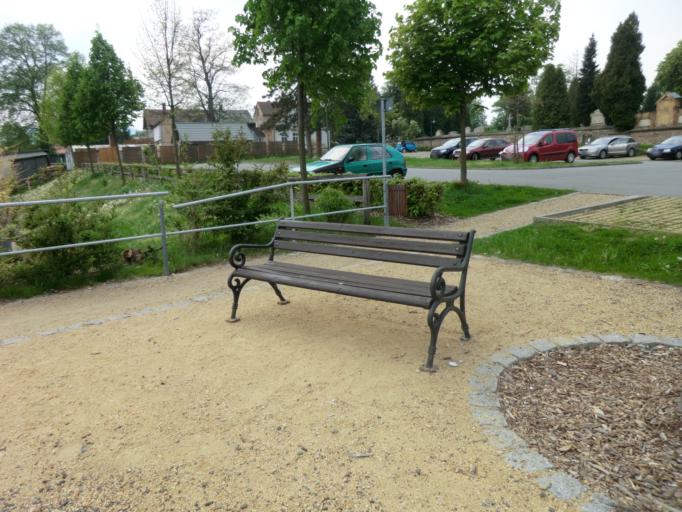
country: DE
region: Saxony
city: Grossschonau
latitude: 50.8983
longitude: 14.6640
